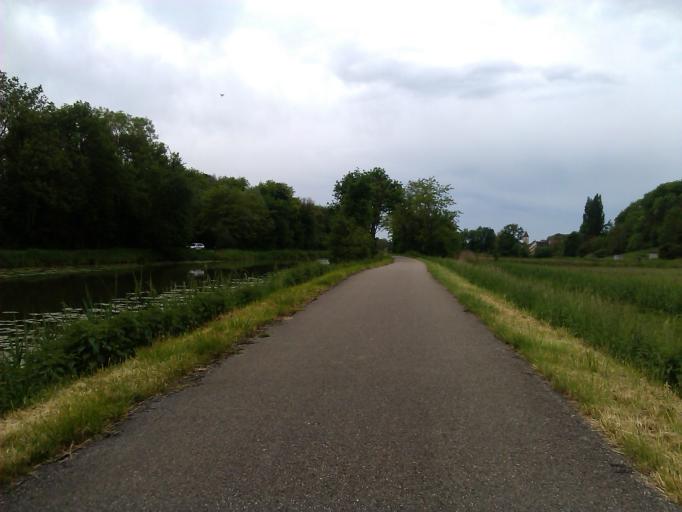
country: FR
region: Franche-Comte
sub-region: Departement du Jura
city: Choisey
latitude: 47.0689
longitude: 5.4670
